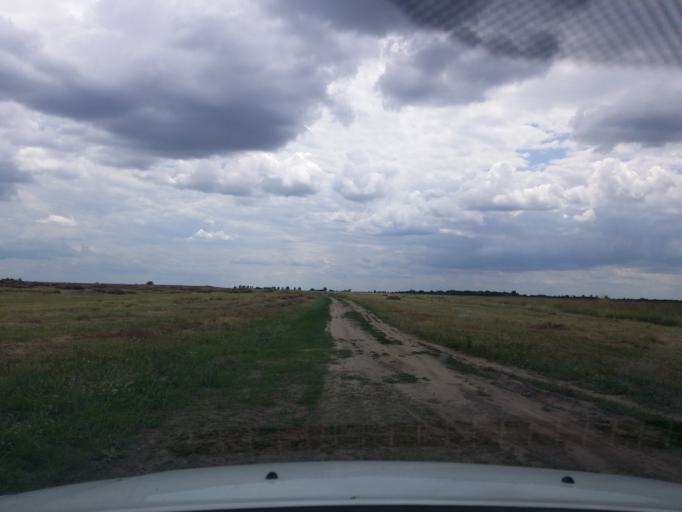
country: HU
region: Hajdu-Bihar
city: Egyek
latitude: 47.5673
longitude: 20.9444
